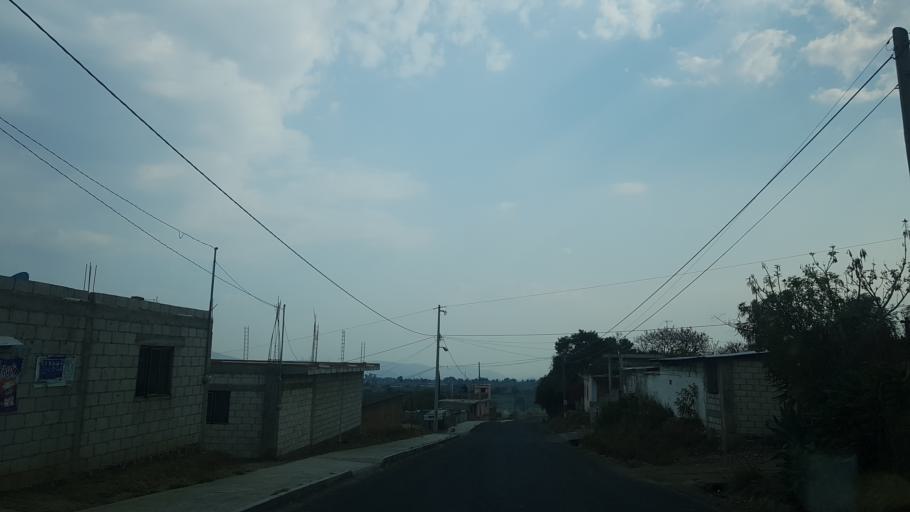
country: MX
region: Puebla
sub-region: Santa Isabel Cholula
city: San Martin Tlamapa
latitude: 18.9710
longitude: -98.3944
